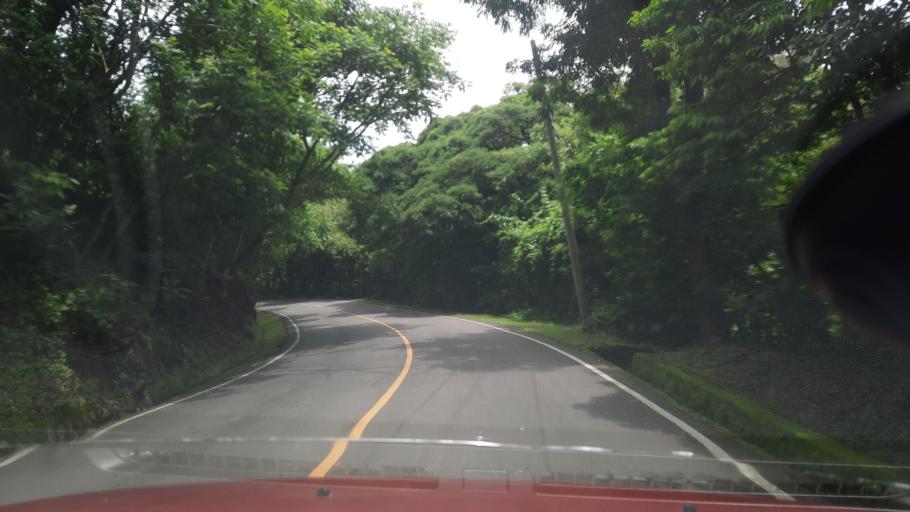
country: SV
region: La Union
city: Santa Rosa de Lima
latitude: 13.6518
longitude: -87.8375
